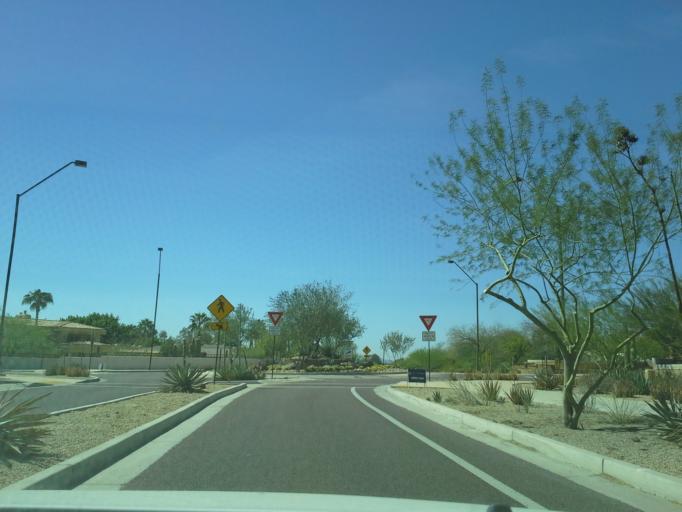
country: US
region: Arizona
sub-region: Maricopa County
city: Scottsdale
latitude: 33.5970
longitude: -111.8474
